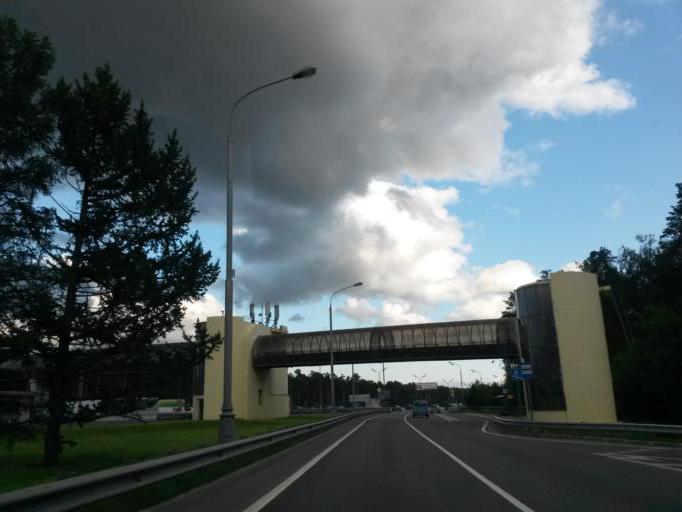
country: RU
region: Moscow
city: Zhulebino
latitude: 55.6848
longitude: 37.8303
